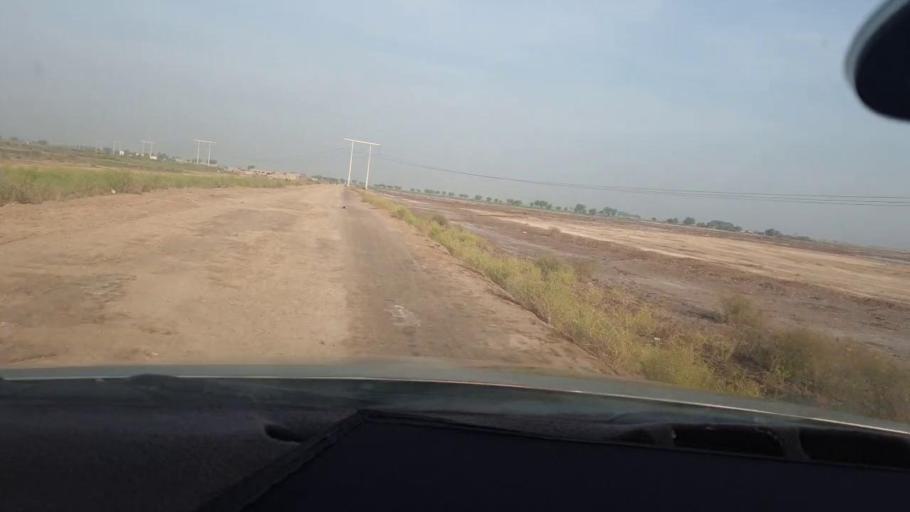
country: PK
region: Sindh
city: Jacobabad
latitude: 28.3347
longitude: 68.4125
